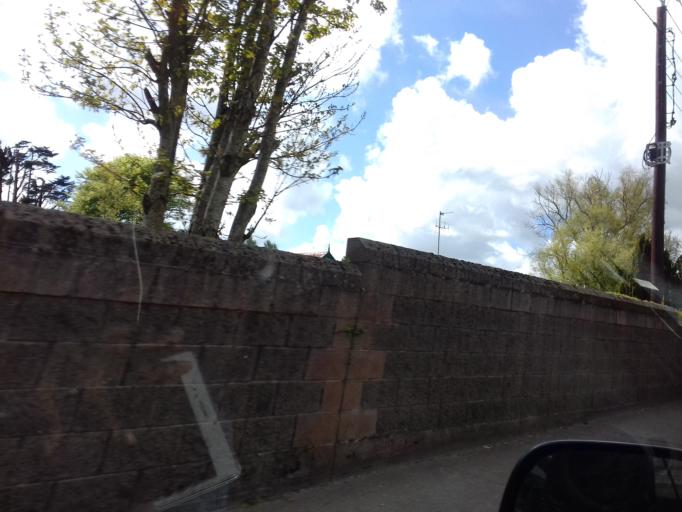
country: IE
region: Leinster
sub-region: Loch Garman
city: Loch Garman
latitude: 52.3281
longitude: -6.4751
